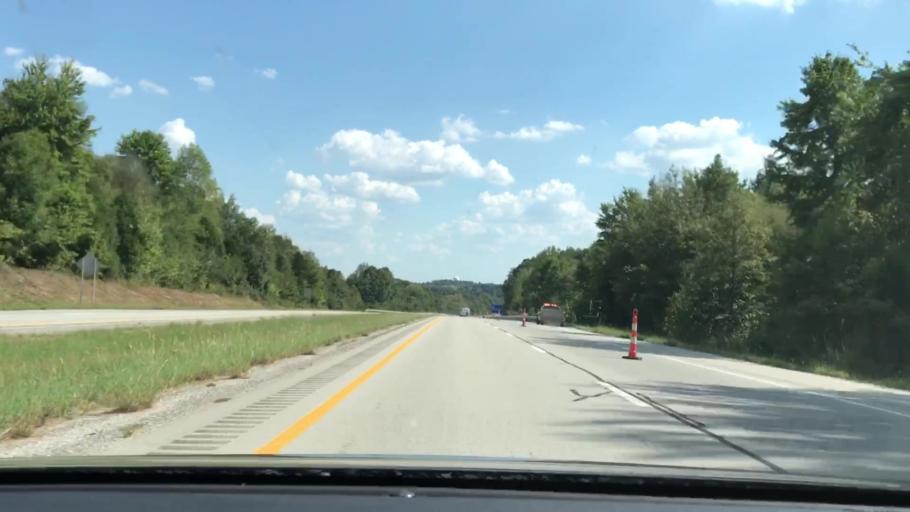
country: US
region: Kentucky
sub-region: Butler County
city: Morgantown
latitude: 37.2247
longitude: -86.7196
